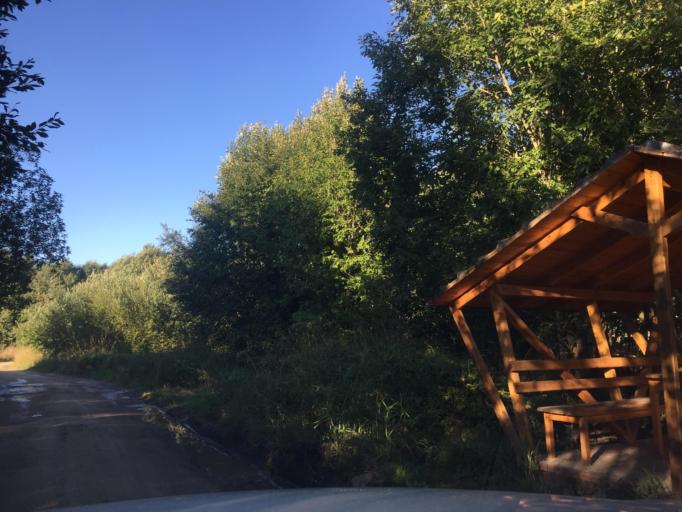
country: RU
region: Leningrad
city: Rozhdestveno
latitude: 59.3279
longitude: 29.9951
